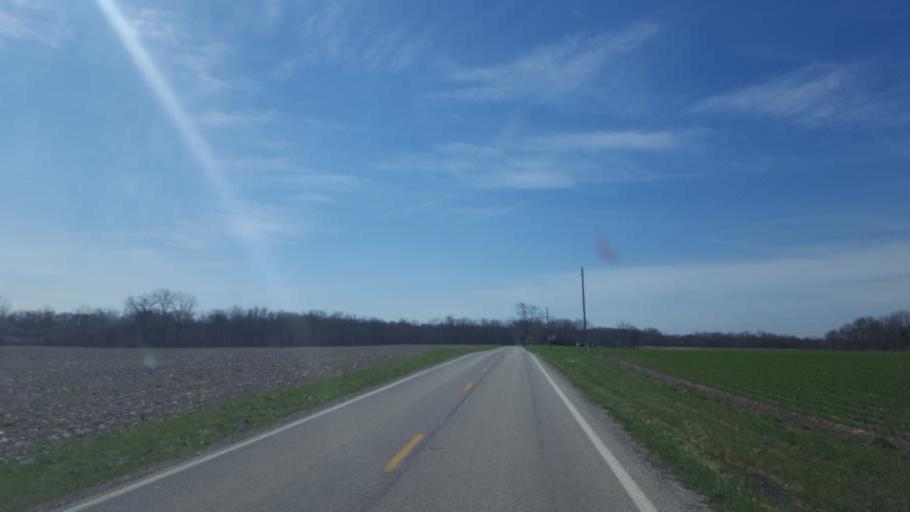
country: US
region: Ohio
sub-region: Delaware County
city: Ashley
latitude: 40.4582
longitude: -82.9635
